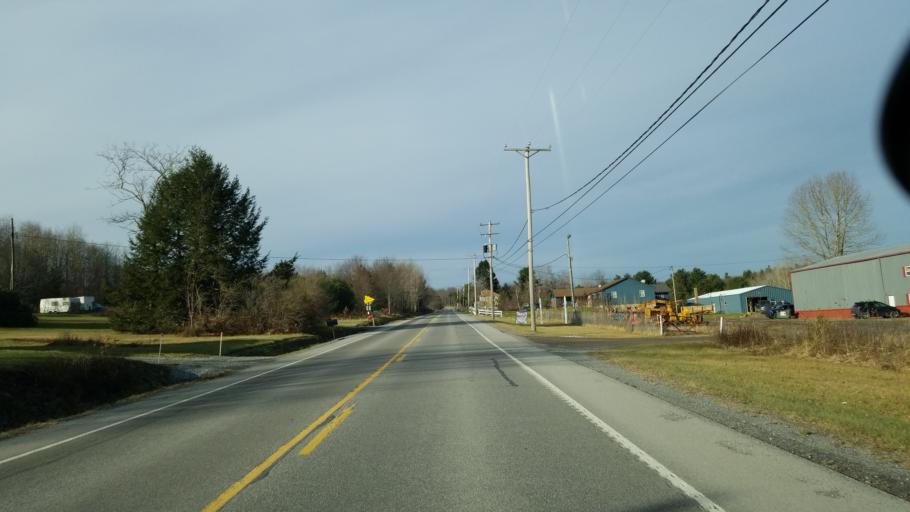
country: US
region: Pennsylvania
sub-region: Clearfield County
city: Curwensville
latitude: 41.0021
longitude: -78.6354
